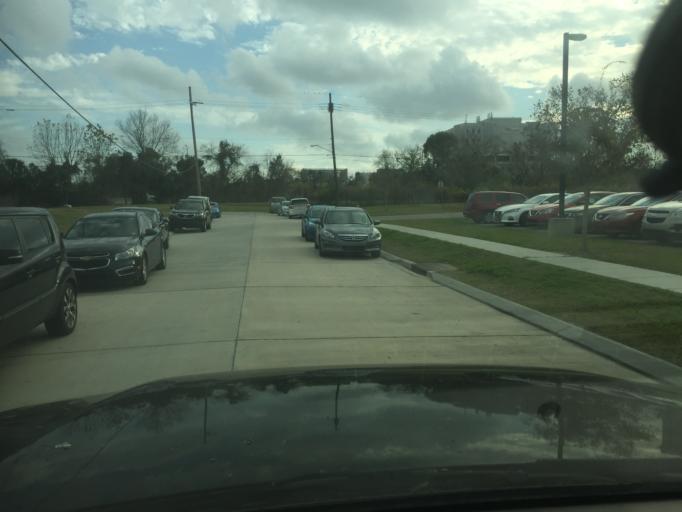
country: US
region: Louisiana
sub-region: Orleans Parish
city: New Orleans
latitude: 29.9941
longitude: -90.0828
